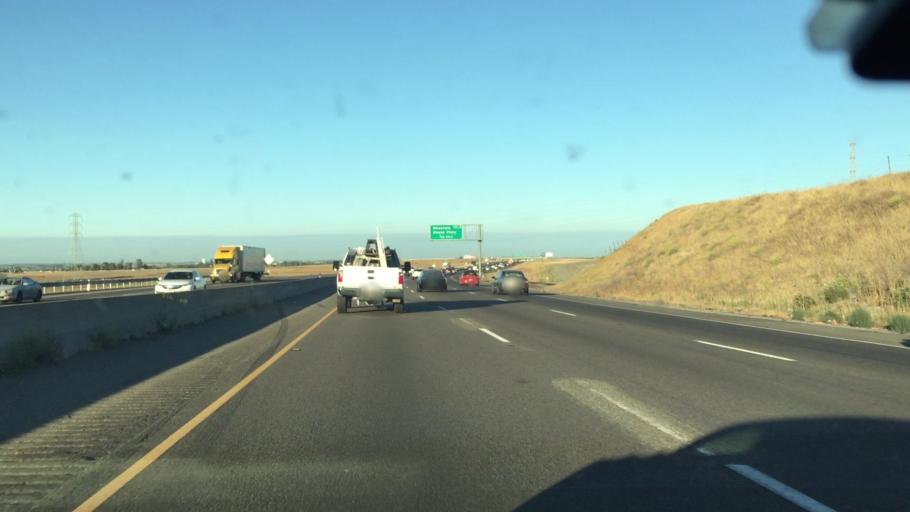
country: US
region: California
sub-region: San Joaquin County
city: Mountain House
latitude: 37.7444
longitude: -121.5517
